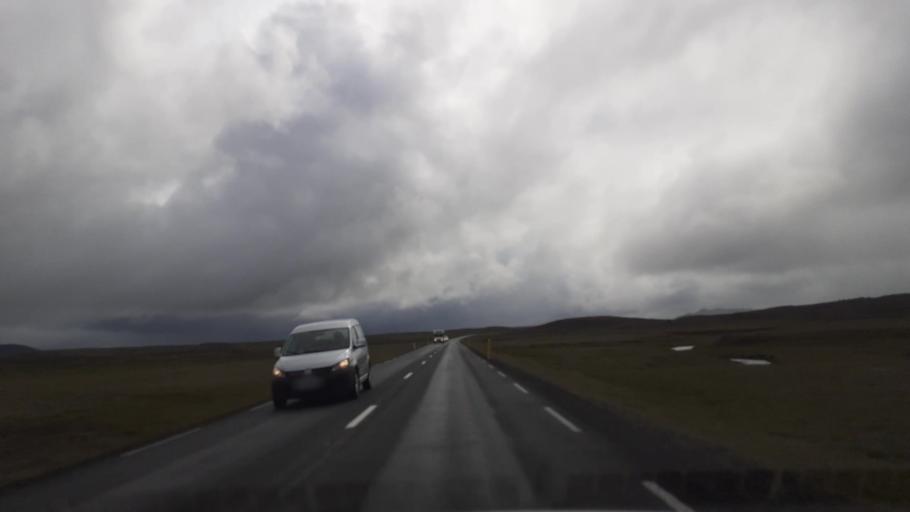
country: IS
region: East
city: Egilsstadir
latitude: 65.3327
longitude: -15.3718
